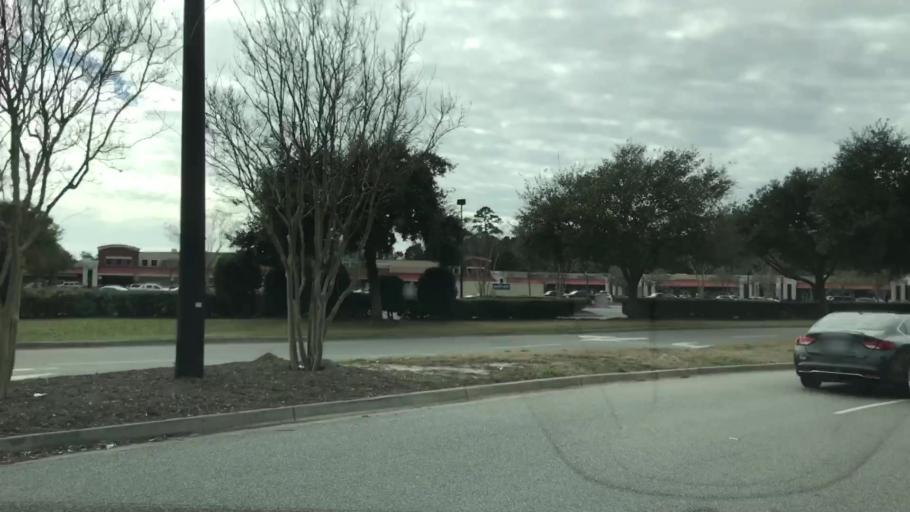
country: US
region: South Carolina
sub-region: Horry County
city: Myrtle Beach
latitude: 33.7265
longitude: -78.8688
